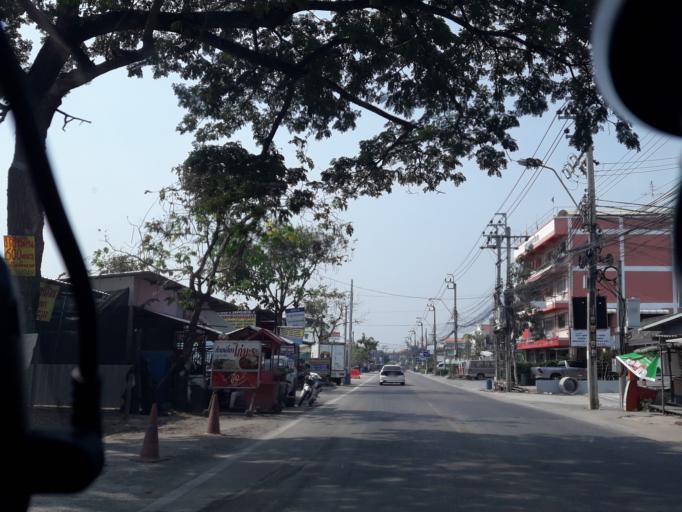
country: TH
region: Bangkok
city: Khlong Sam Wa
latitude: 13.8416
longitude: 100.7160
